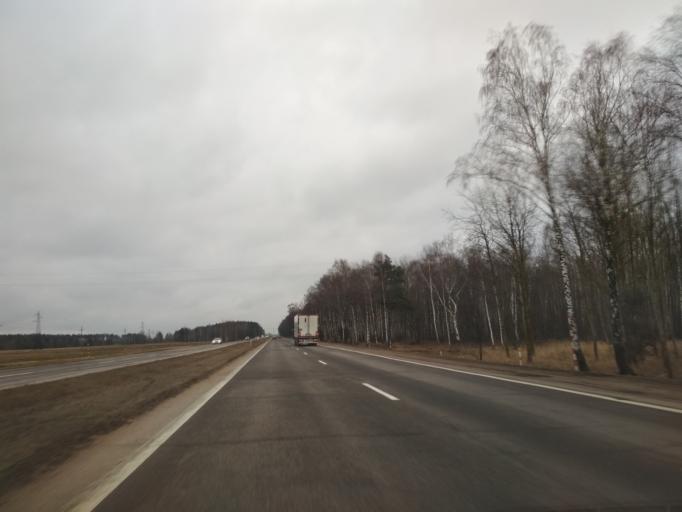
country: BY
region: Minsk
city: Dukora
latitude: 53.6287
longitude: 28.0274
